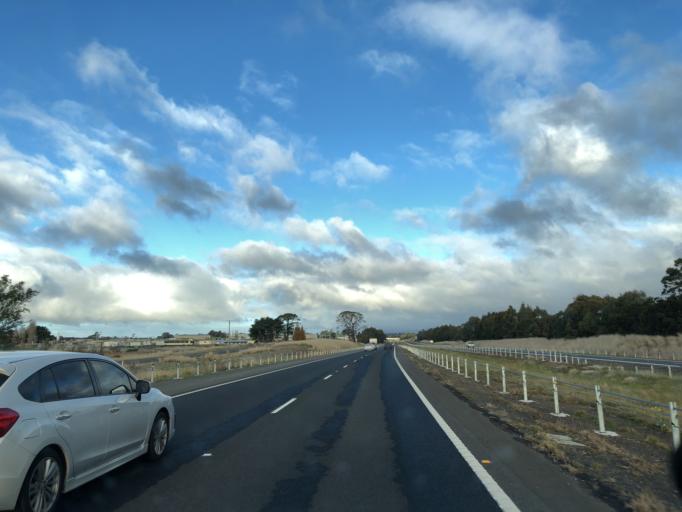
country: AU
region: Victoria
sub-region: Mount Alexander
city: Castlemaine
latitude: -37.2295
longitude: 144.4445
